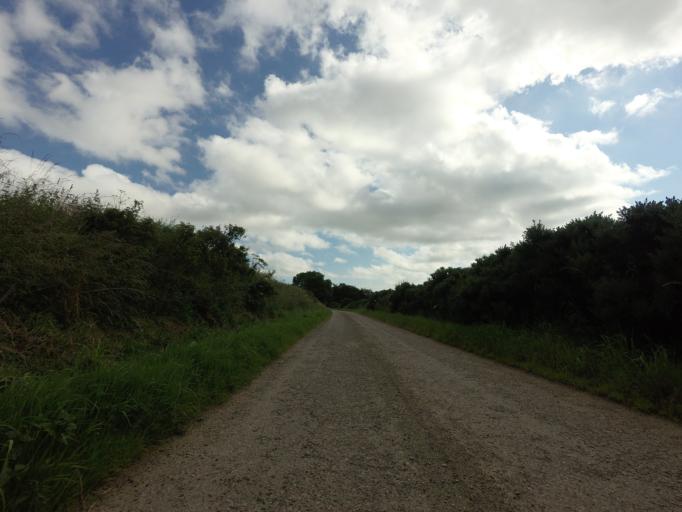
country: GB
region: Scotland
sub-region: Aberdeenshire
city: Banff
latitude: 57.5991
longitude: -2.5121
